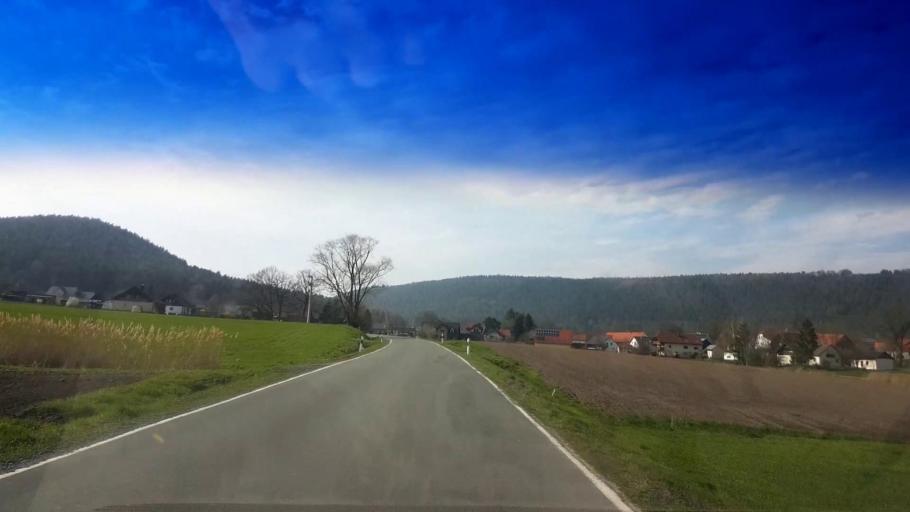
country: DE
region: Bavaria
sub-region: Upper Franconia
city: Trebgast
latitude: 50.0543
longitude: 11.5148
